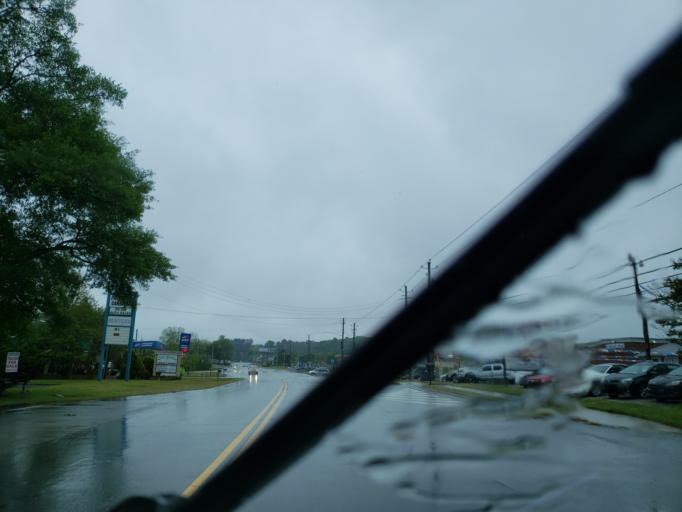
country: US
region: Georgia
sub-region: Carroll County
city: Villa Rica
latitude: 33.7304
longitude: -84.9418
